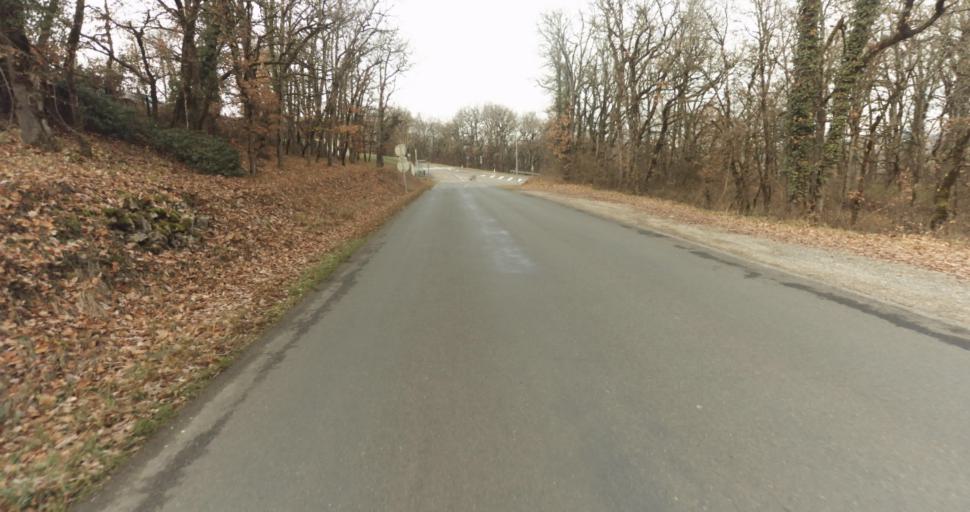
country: FR
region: Midi-Pyrenees
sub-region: Departement du Lot
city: Figeac
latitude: 44.6133
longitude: 2.0112
